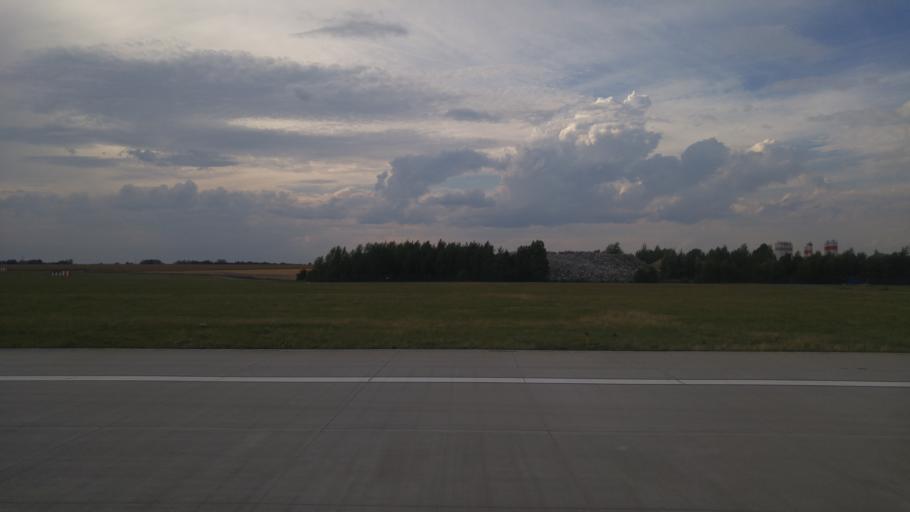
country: CZ
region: Central Bohemia
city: Hostivice
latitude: 50.1082
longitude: 14.2472
